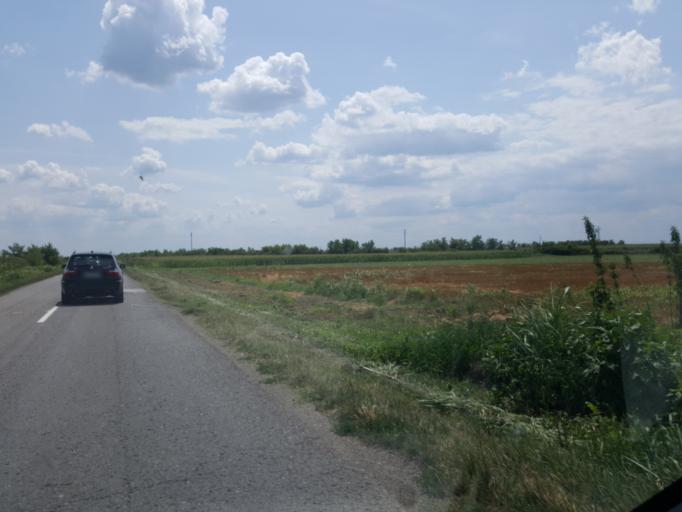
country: RS
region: Autonomna Pokrajina Vojvodina
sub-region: Sremski Okrug
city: Pecinci
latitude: 44.8805
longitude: 19.9606
